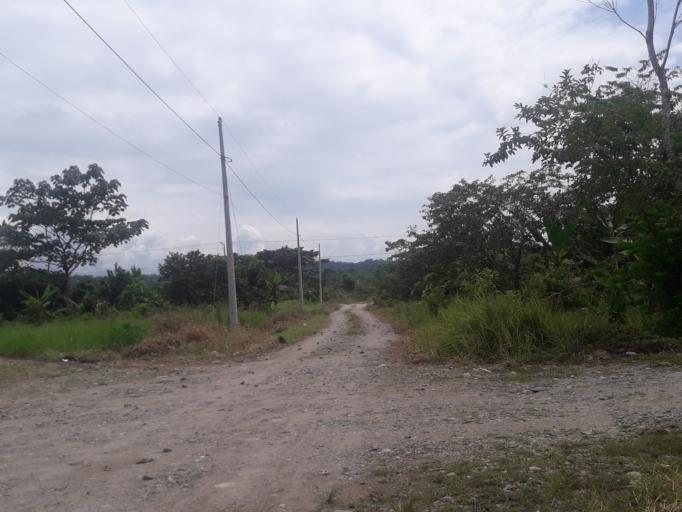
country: EC
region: Napo
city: Tena
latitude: -1.0593
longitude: -77.7957
